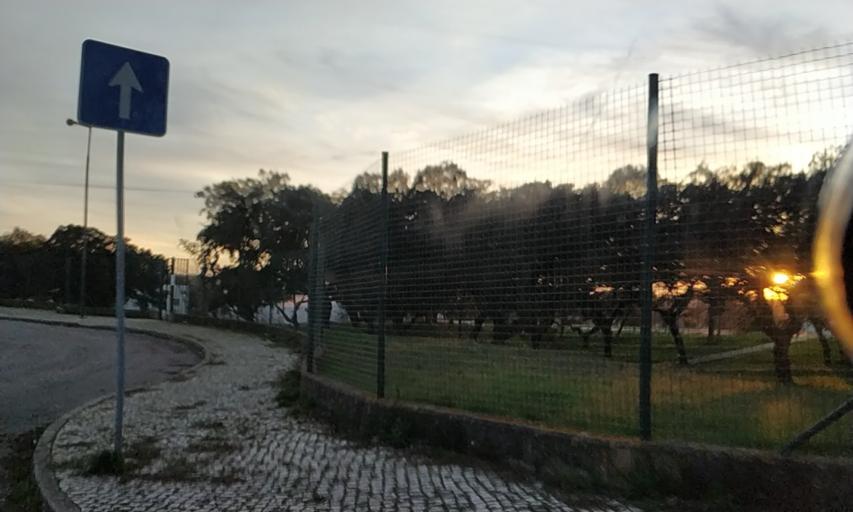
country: PT
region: Setubal
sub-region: Setubal
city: Setubal
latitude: 38.5218
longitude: -8.8372
